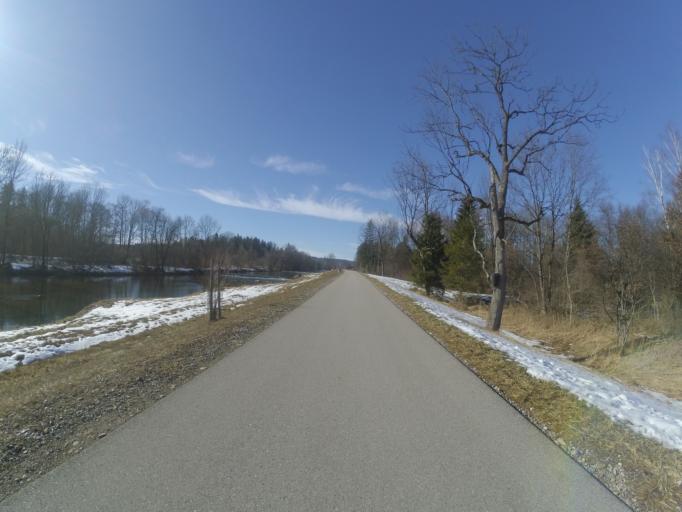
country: DE
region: Bavaria
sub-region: Upper Bavaria
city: Vagen
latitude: 47.8913
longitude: 11.8686
